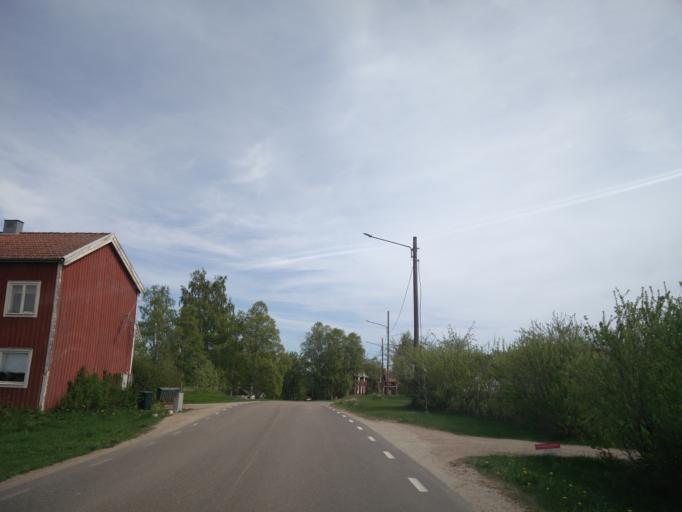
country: SE
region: Gaevleborg
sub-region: Hudiksvalls Kommun
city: Sorforsa
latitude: 61.7672
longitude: 17.0038
